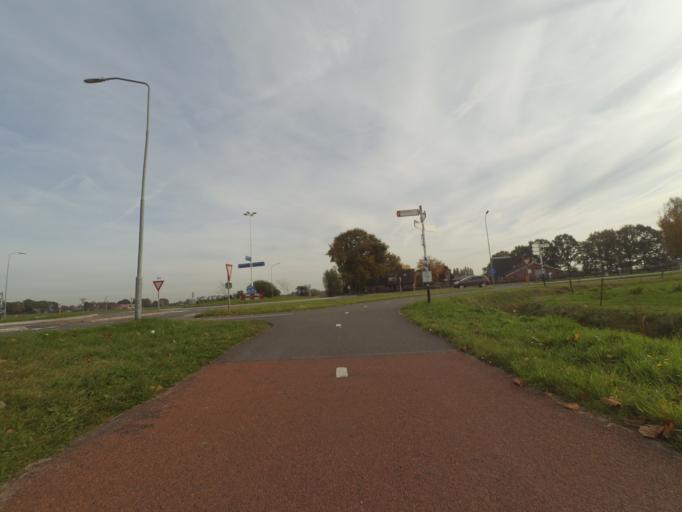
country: NL
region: Gelderland
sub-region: Gemeente Barneveld
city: Barneveld
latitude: 52.1192
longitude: 5.5408
